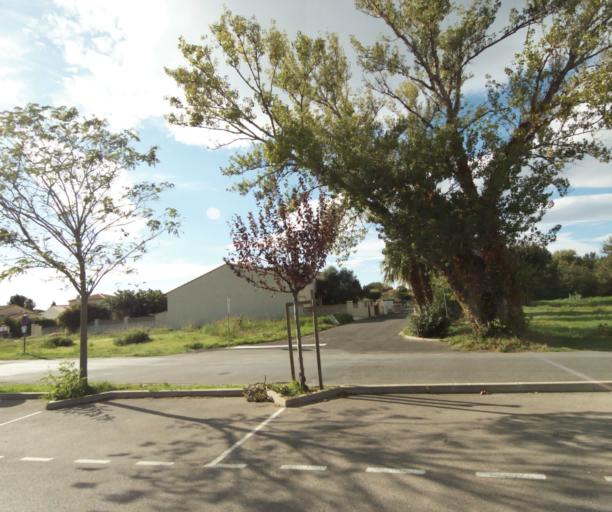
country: FR
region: Languedoc-Roussillon
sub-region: Departement des Pyrenees-Orientales
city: Argelers
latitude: 42.5450
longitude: 3.0370
